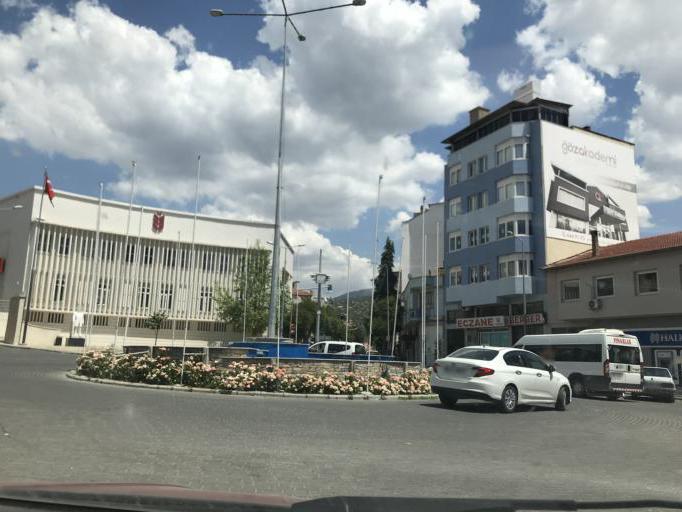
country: TR
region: Denizli
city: Tavas
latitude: 37.5730
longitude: 29.0706
